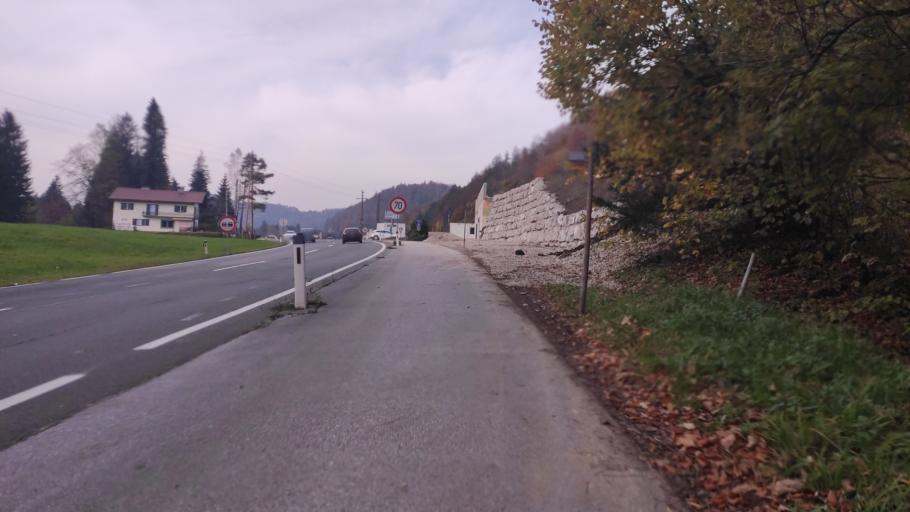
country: AT
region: Salzburg
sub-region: Politischer Bezirk Salzburg-Umgebung
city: Ebenau
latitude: 47.7800
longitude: 13.1814
